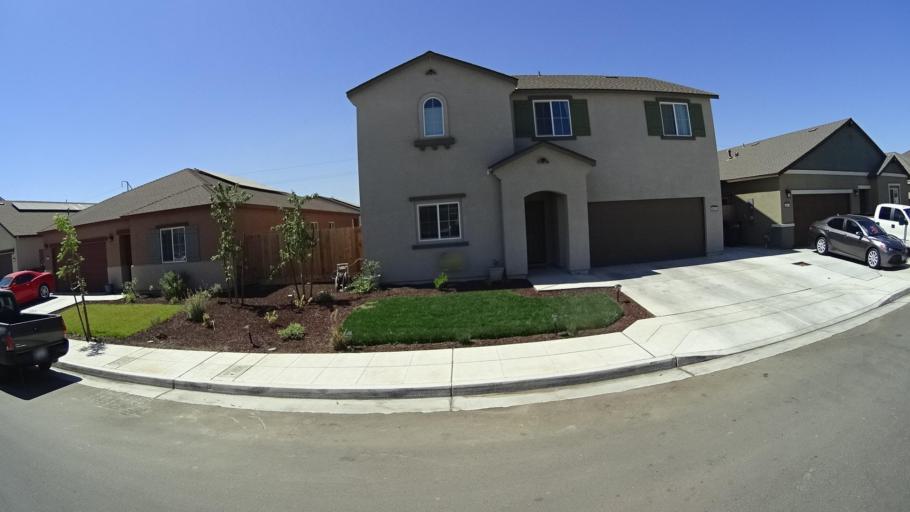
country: US
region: California
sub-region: Fresno County
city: Sunnyside
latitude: 36.7231
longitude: -119.6706
